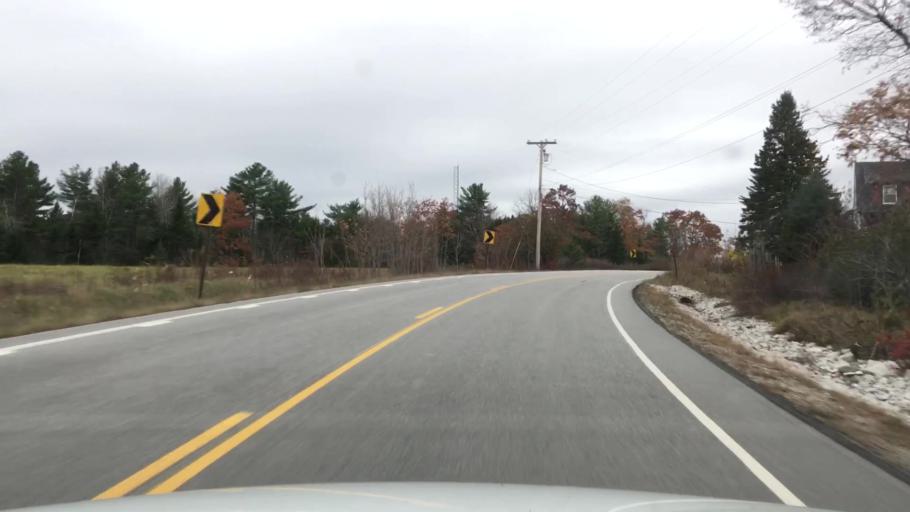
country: US
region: Maine
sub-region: Hancock County
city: Orland
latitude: 44.5306
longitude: -68.6744
